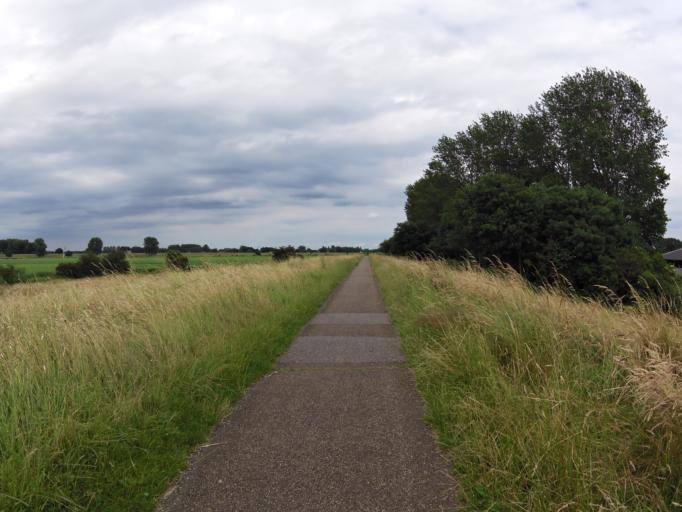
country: NL
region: North Brabant
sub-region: Gemeente Grave
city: Grave
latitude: 51.7696
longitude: 5.7218
